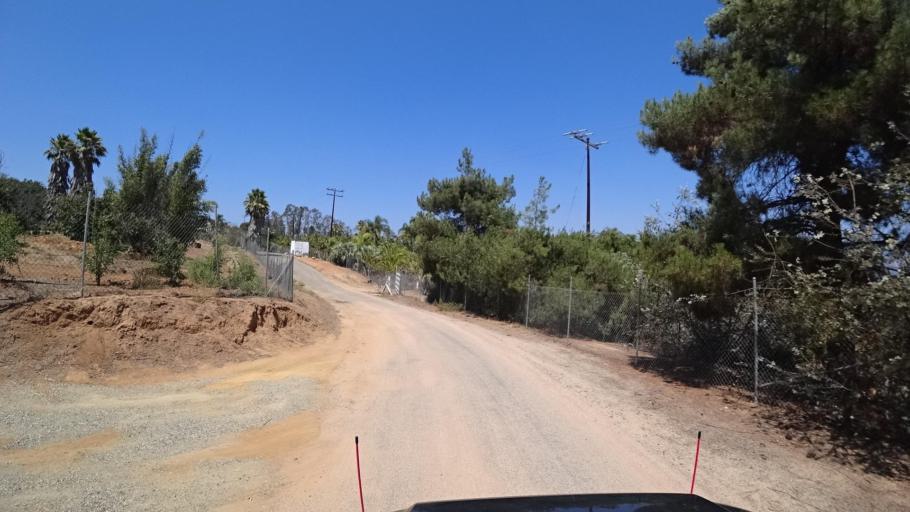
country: US
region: California
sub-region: San Diego County
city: Fallbrook
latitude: 33.4537
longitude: -117.2653
